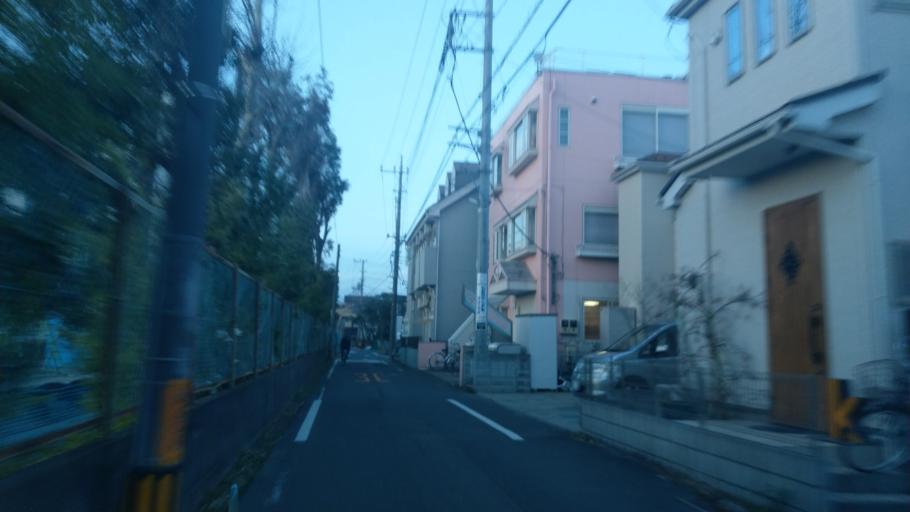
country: JP
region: Saitama
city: Yono
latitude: 35.8707
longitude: 139.6040
